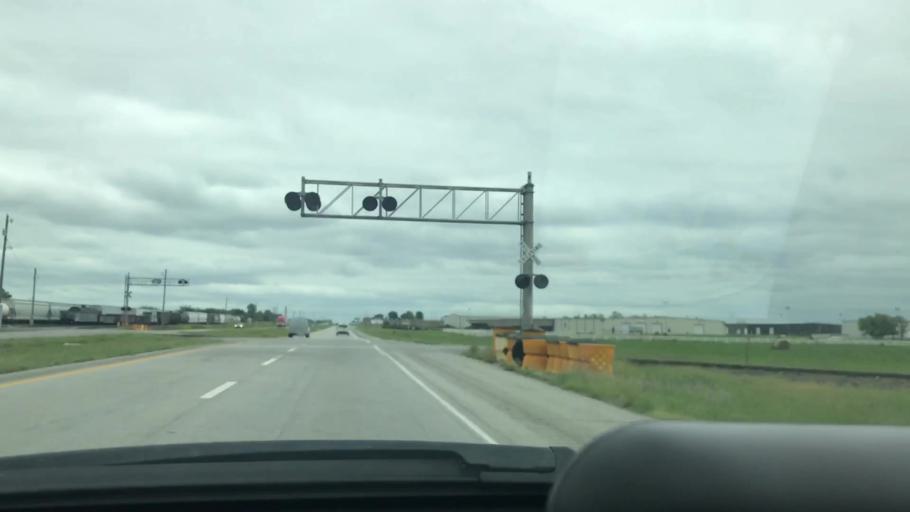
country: US
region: Oklahoma
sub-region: Mayes County
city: Chouteau
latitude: 36.2367
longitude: -95.3382
